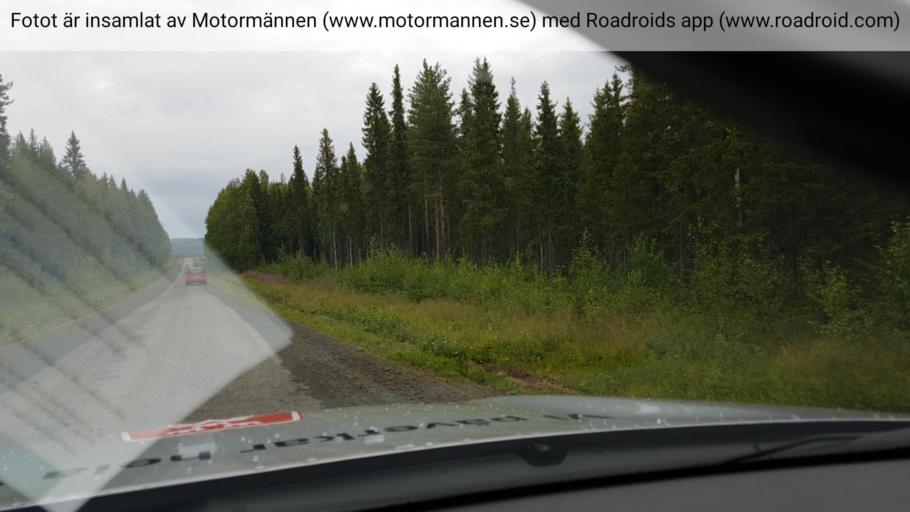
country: SE
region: Norrbotten
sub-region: Alvsbyns Kommun
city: AElvsbyn
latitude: 65.9746
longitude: 21.2172
